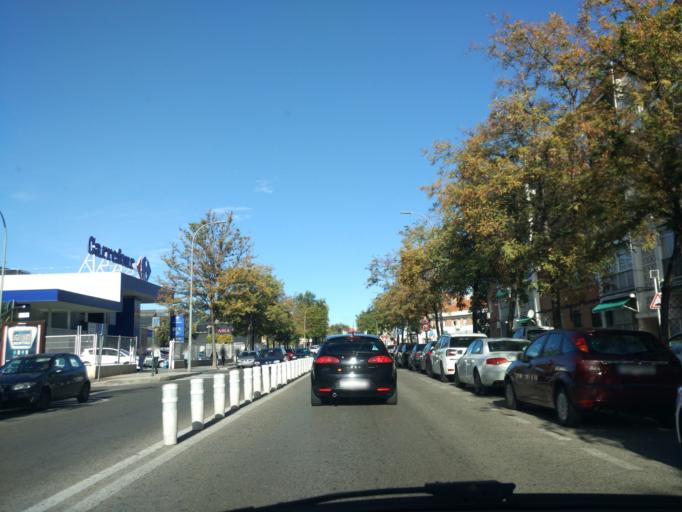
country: ES
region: Madrid
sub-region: Provincia de Madrid
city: Torrejon de Ardoz
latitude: 40.4497
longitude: -3.4699
